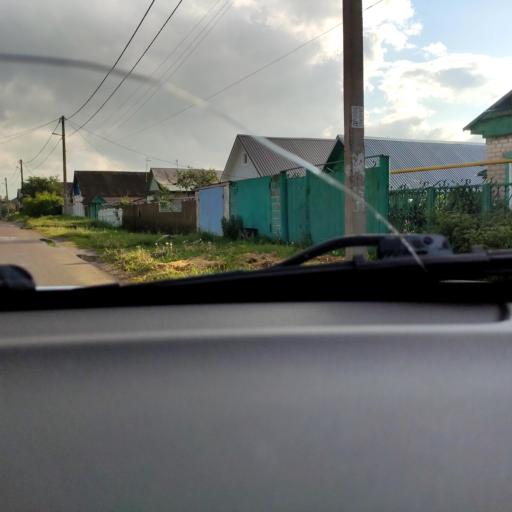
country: RU
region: Tatarstan
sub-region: Gorod Kazan'
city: Kazan
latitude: 55.8545
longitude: 49.1904
